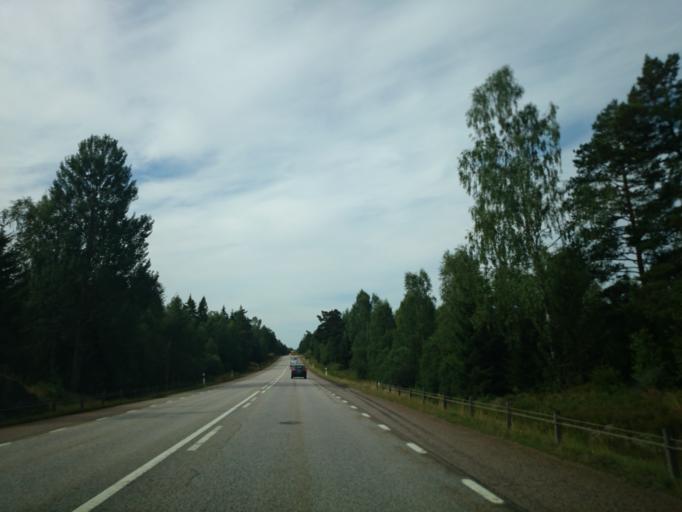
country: SE
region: Kalmar
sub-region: Oskarshamns Kommun
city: Oskarshamn
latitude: 57.4549
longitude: 16.5118
